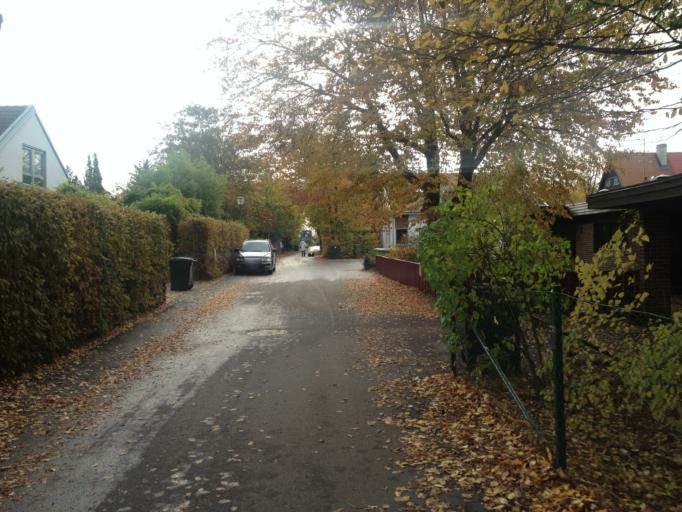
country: SE
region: Skane
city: Bjarred
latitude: 55.7200
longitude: 13.0126
